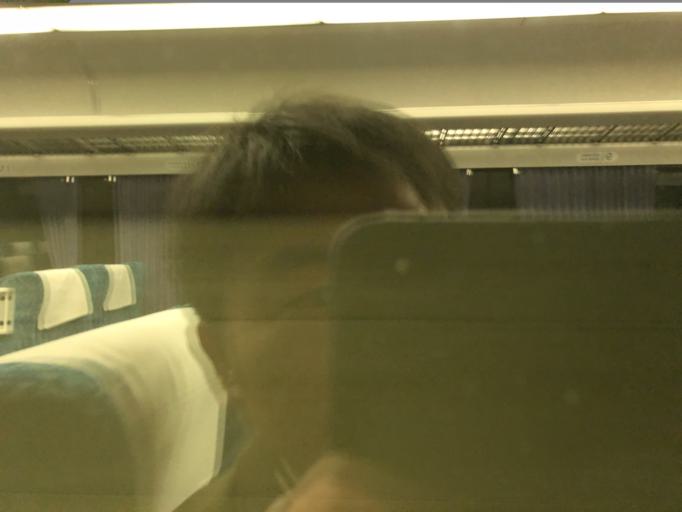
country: JP
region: Kochi
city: Nakamura
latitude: 33.0714
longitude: 133.1040
